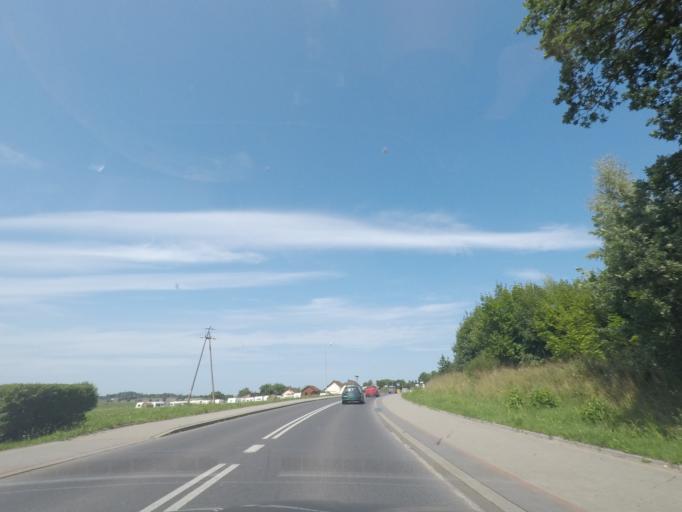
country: PL
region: West Pomeranian Voivodeship
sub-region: Powiat koszalinski
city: Sianow
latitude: 54.2493
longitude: 16.2813
